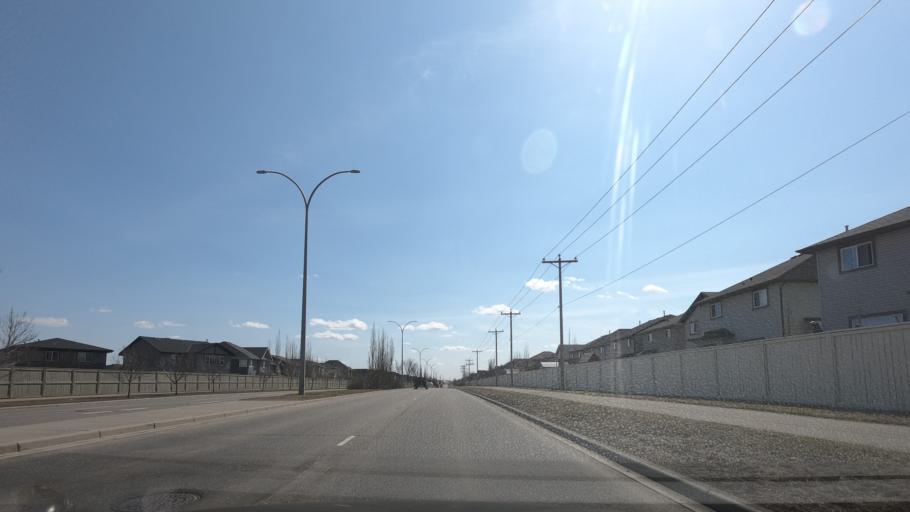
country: CA
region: Alberta
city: Airdrie
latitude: 51.2653
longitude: -114.0251
